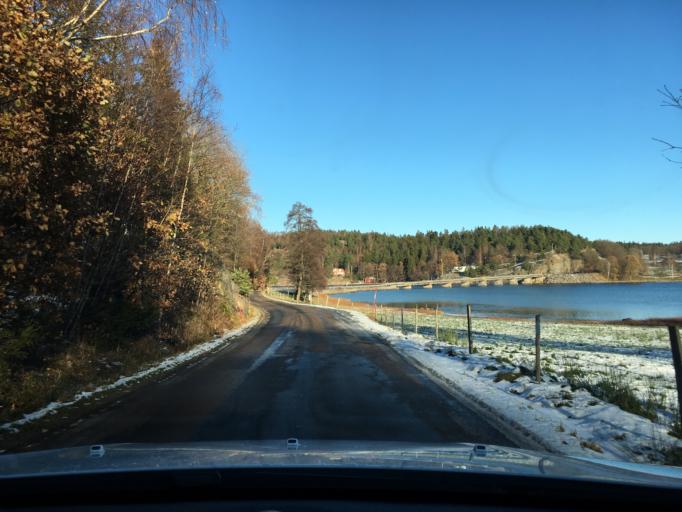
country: SE
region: Vaestra Goetaland
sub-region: Tjorns Kommun
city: Myggenas
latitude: 58.0922
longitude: 11.7551
